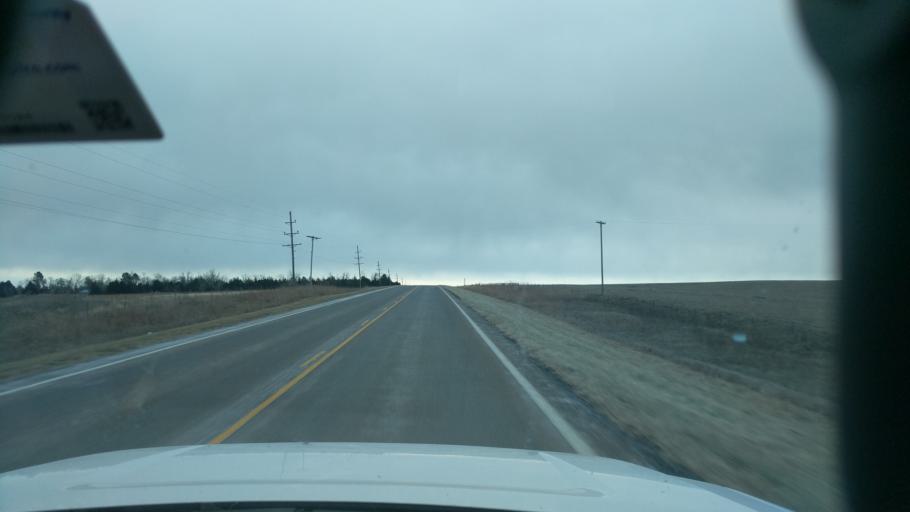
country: US
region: Kansas
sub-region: Marion County
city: Hillsboro
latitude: 38.3405
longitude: -97.3347
